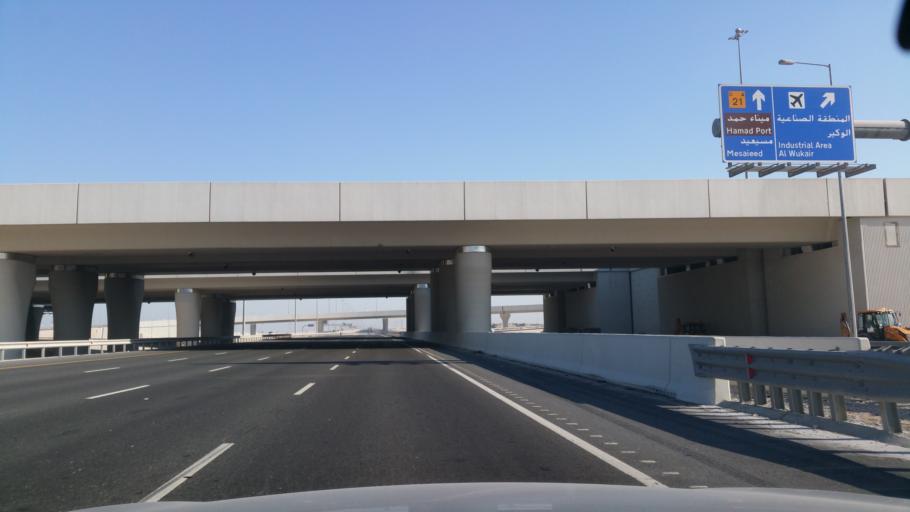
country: QA
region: Al Wakrah
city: Al Wukayr
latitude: 25.1230
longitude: 51.4865
